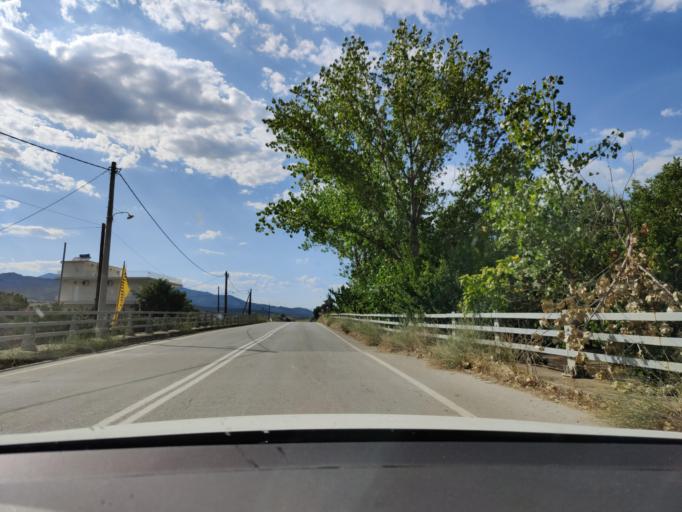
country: GR
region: Central Macedonia
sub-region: Nomos Serron
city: Strymoniko
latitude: 41.0917
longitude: 23.2779
